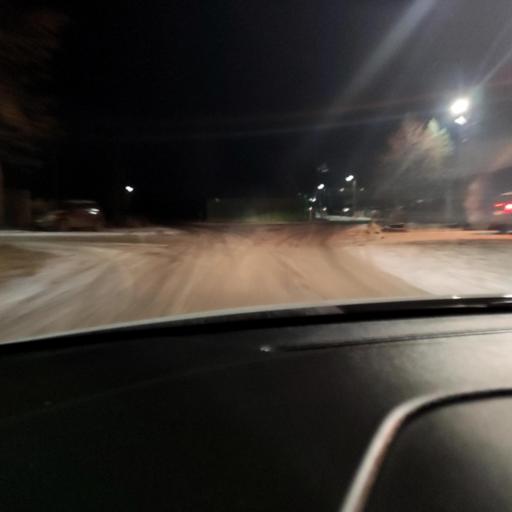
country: RU
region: Tatarstan
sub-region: Gorod Kazan'
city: Kazan
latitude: 55.7208
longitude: 49.0980
